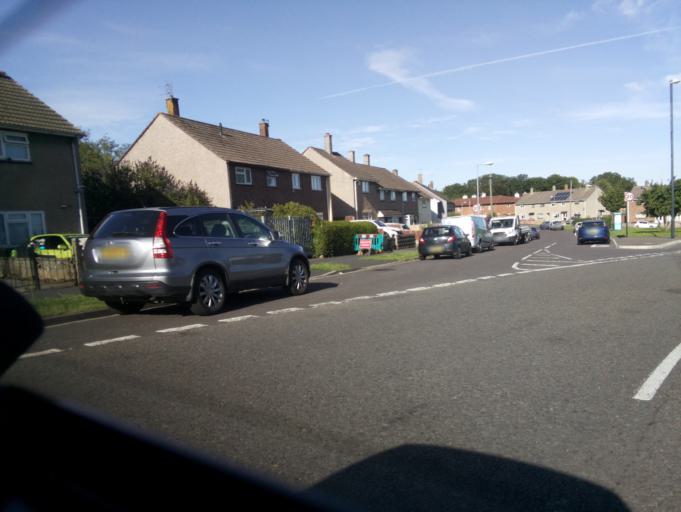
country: GB
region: England
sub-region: Bath and North East Somerset
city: Whitchurch
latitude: 51.4104
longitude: -2.5527
